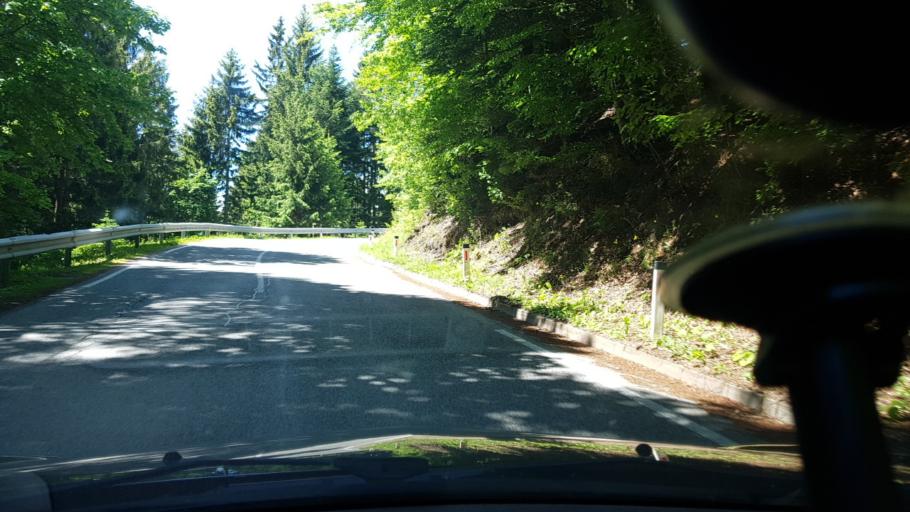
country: SI
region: Zrece
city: Zrece
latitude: 46.4315
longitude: 15.3706
